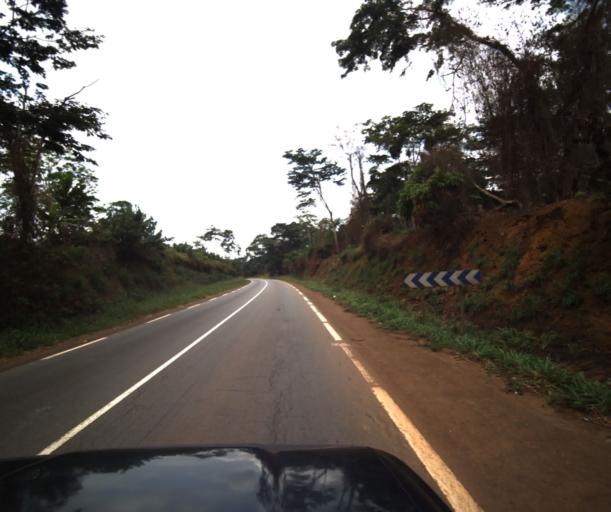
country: CM
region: Centre
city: Eseka
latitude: 3.8698
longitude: 10.9160
